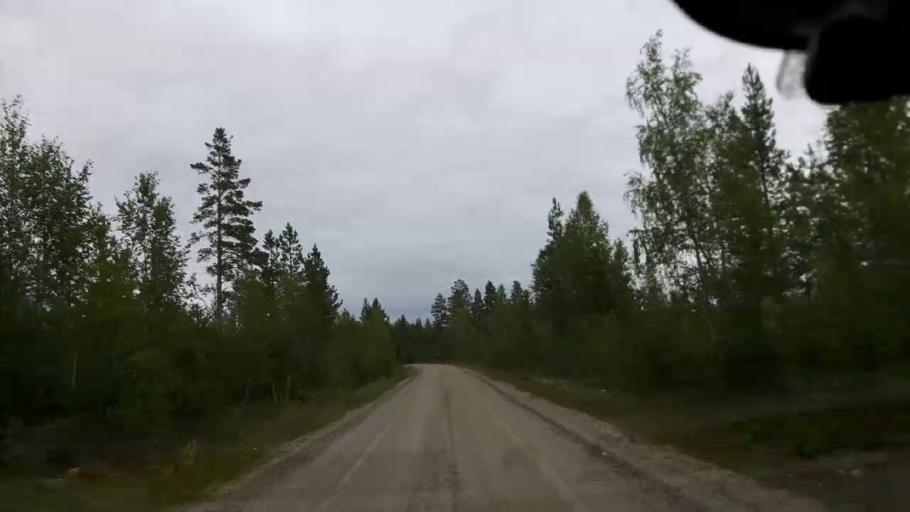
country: SE
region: Vaesternorrland
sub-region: Ange Kommun
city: Ange
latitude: 62.8124
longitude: 15.7229
